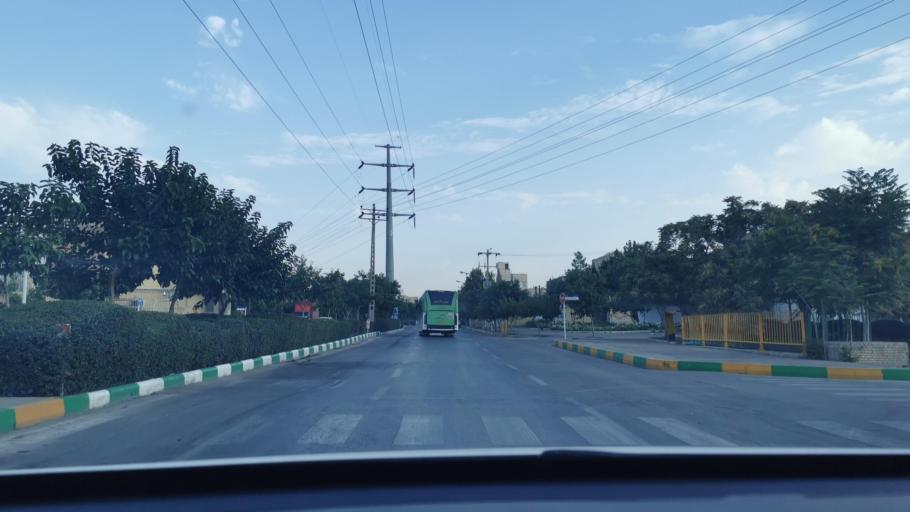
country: IR
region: Razavi Khorasan
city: Mashhad
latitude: 36.3542
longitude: 59.5278
